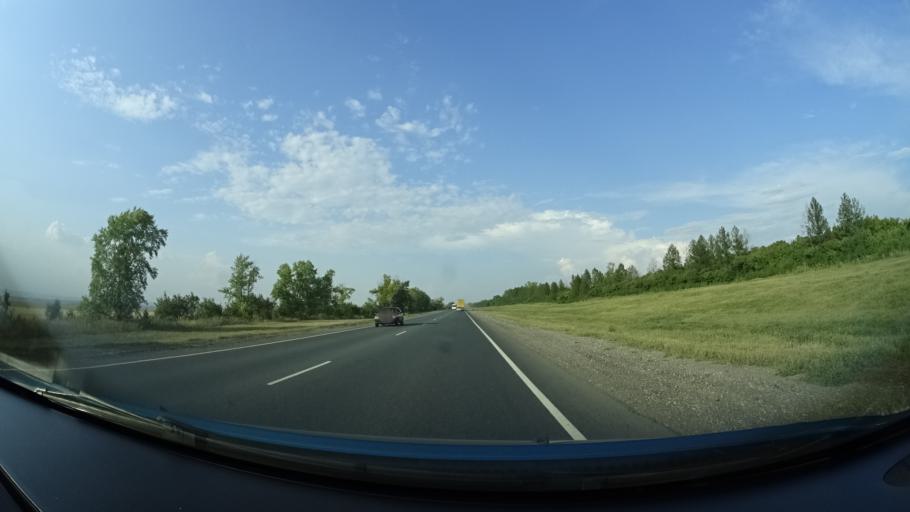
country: RU
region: Samara
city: Krasnyy Yar
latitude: 53.6430
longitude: 50.7328
